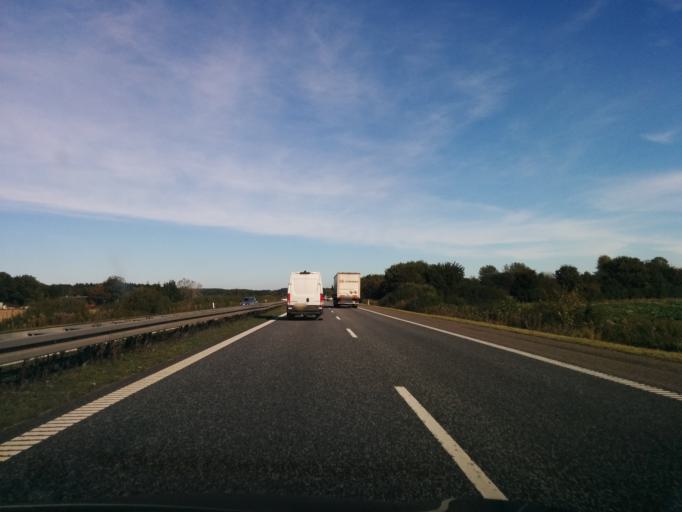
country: DK
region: South Denmark
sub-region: Fredericia Kommune
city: Taulov
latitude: 55.5718
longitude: 9.5640
